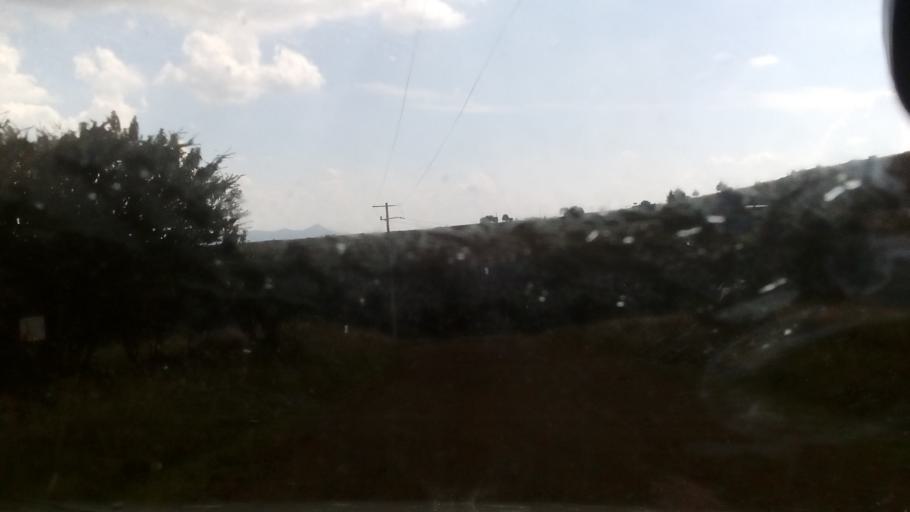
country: MX
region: Guanajuato
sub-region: Silao de la Victoria
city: San Francisco (Banos de Agua Caliente)
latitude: 21.1517
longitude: -101.4351
